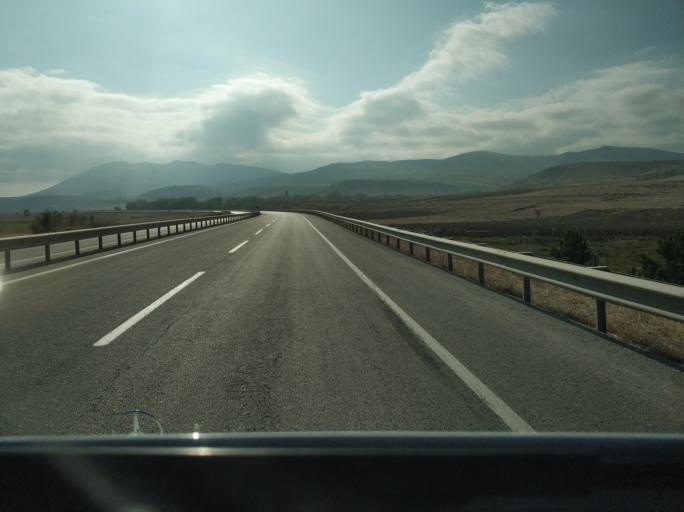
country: TR
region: Sivas
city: Yildizeli
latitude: 39.8489
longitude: 36.5152
